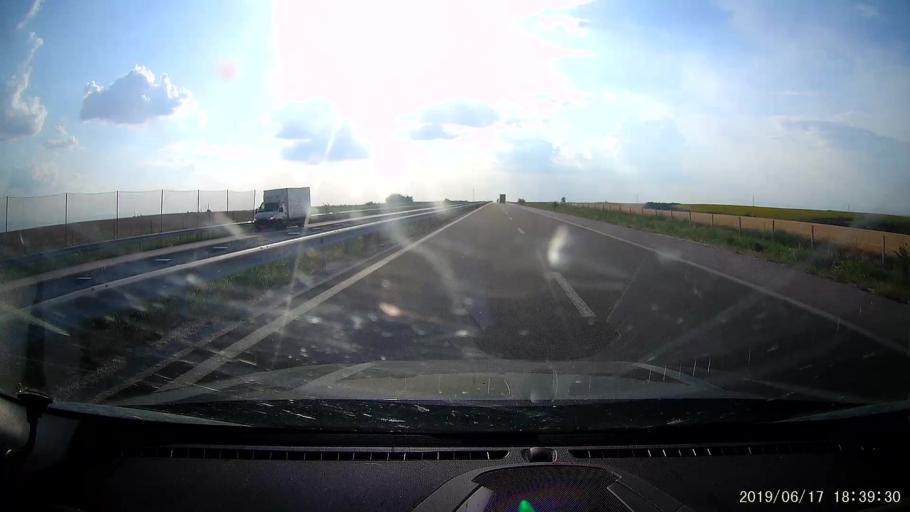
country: BG
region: Stara Zagora
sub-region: Obshtina Chirpan
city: Chirpan
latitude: 42.1457
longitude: 25.3055
